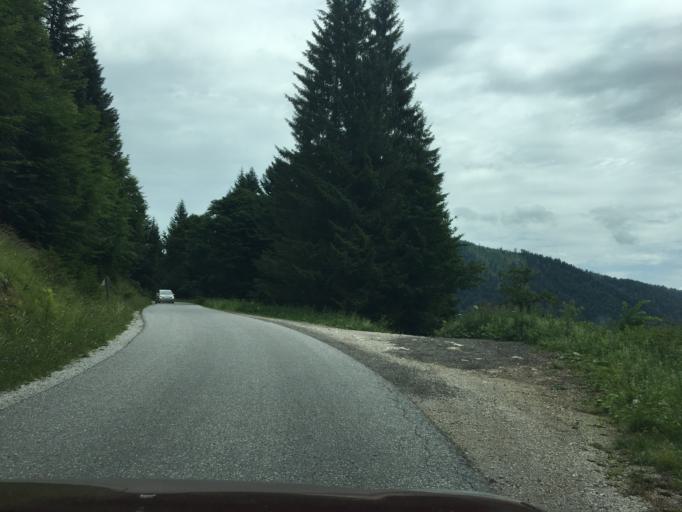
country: AT
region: Salzburg
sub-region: Politischer Bezirk Hallein
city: Abtenau
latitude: 47.6087
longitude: 13.3829
